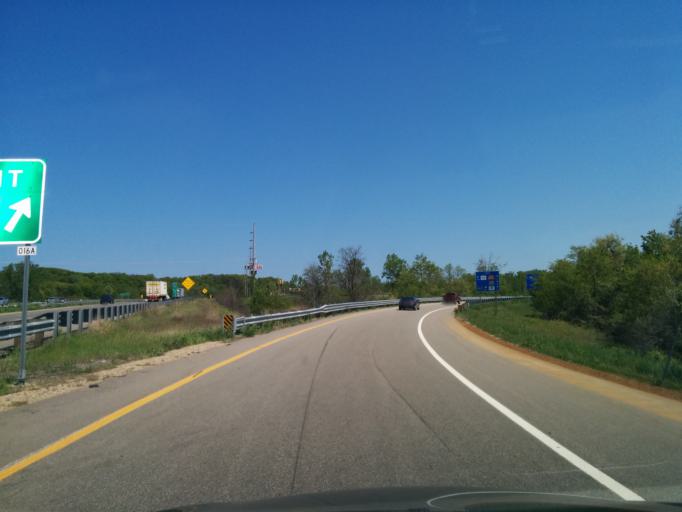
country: US
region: Michigan
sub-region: Berrien County
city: Bridgman
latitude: 41.9275
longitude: -86.5703
